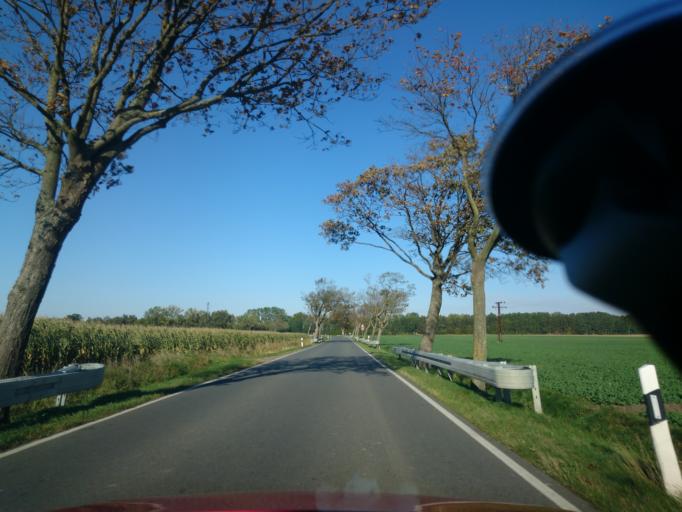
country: DE
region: Mecklenburg-Vorpommern
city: Saal
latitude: 54.3017
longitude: 12.5082
